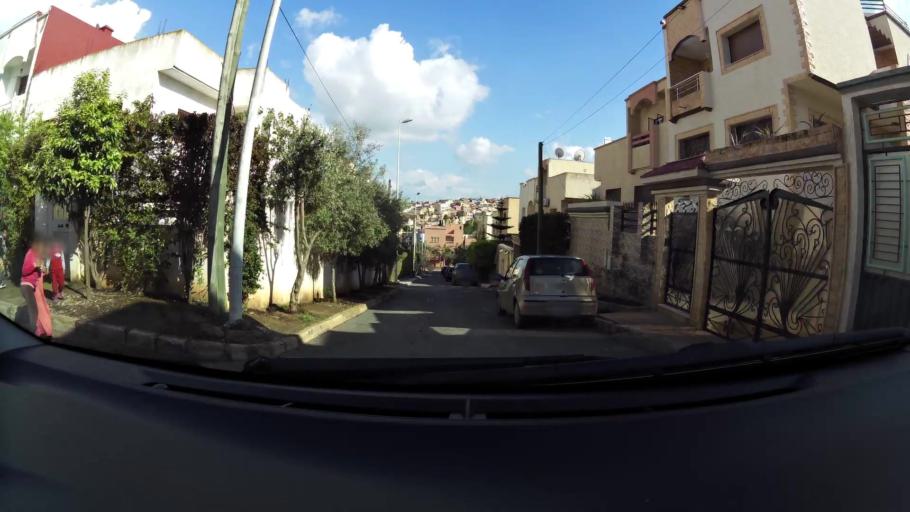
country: MA
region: Chaouia-Ouardigha
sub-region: Settat Province
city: Settat
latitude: 33.0124
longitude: -7.6326
